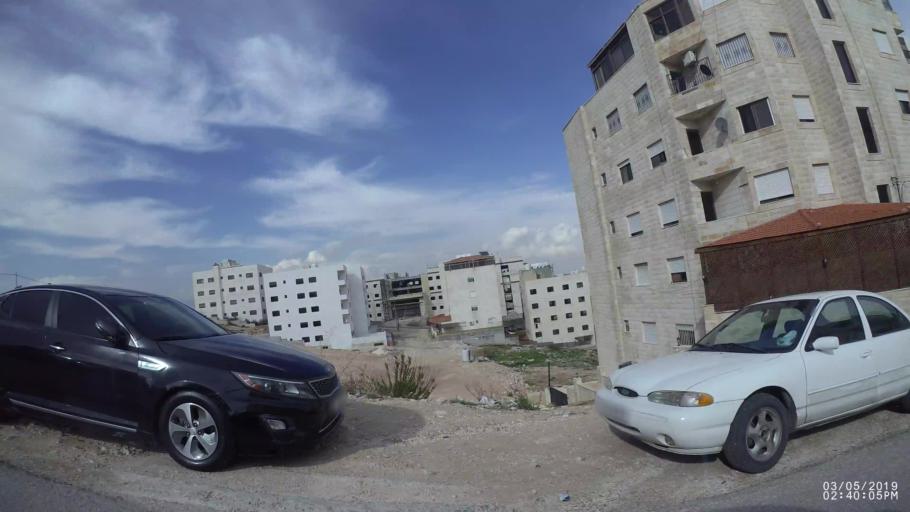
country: JO
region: Amman
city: Amman
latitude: 32.0121
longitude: 35.9381
